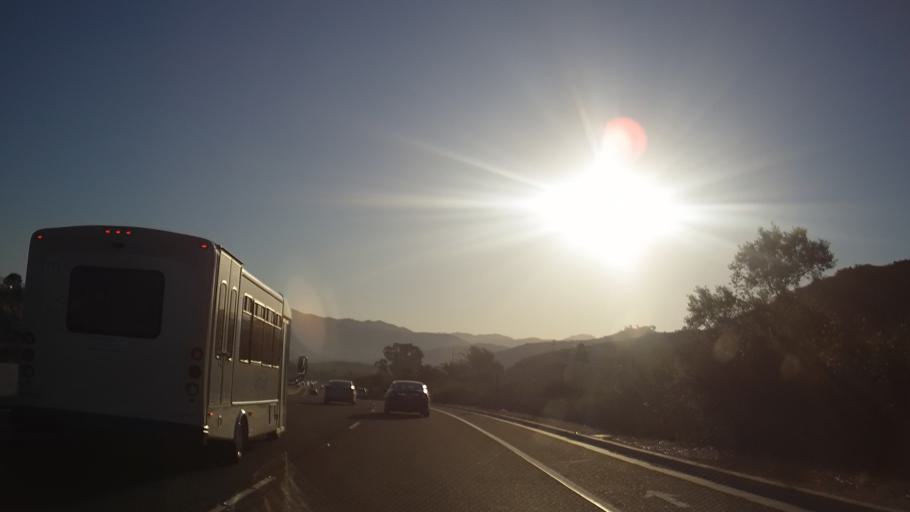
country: US
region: California
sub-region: San Diego County
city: Rancho San Diego
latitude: 32.7391
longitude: -116.9488
